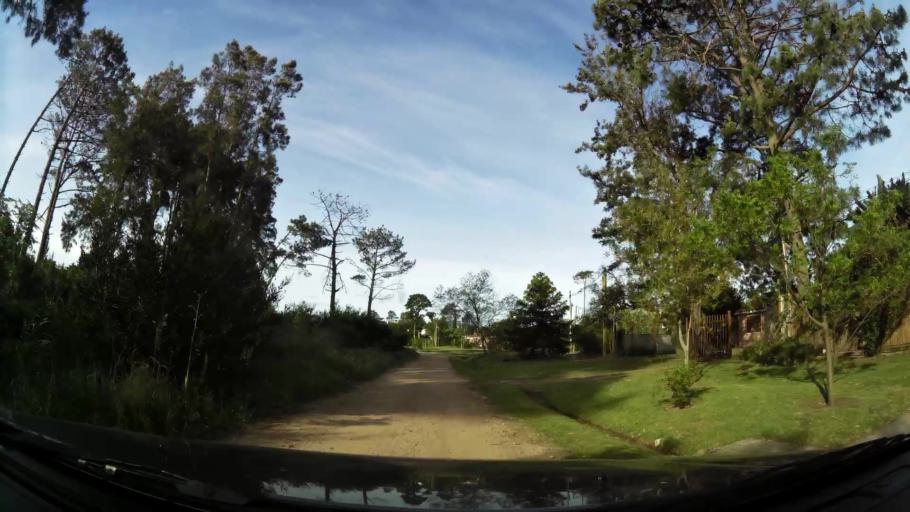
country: UY
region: Canelones
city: Empalme Olmos
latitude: -34.7888
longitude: -55.8570
